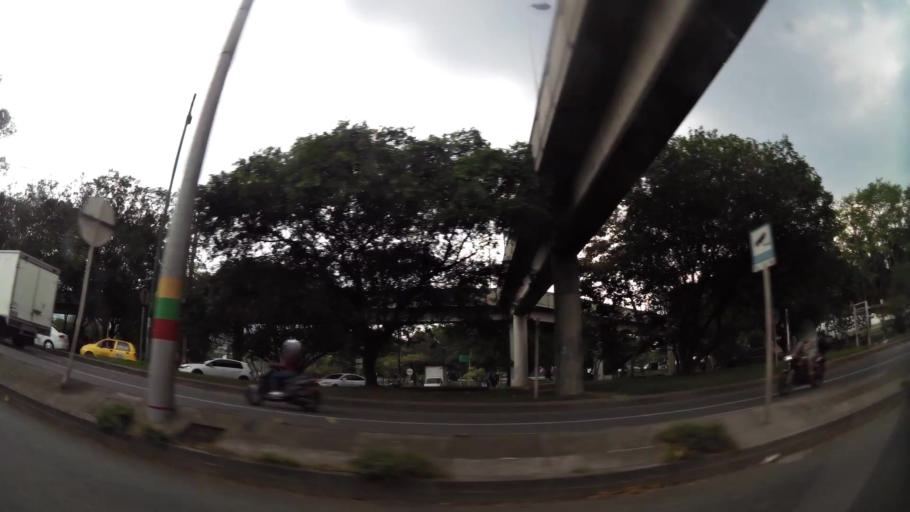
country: CO
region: Antioquia
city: Envigado
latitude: 6.1763
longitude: -75.5970
